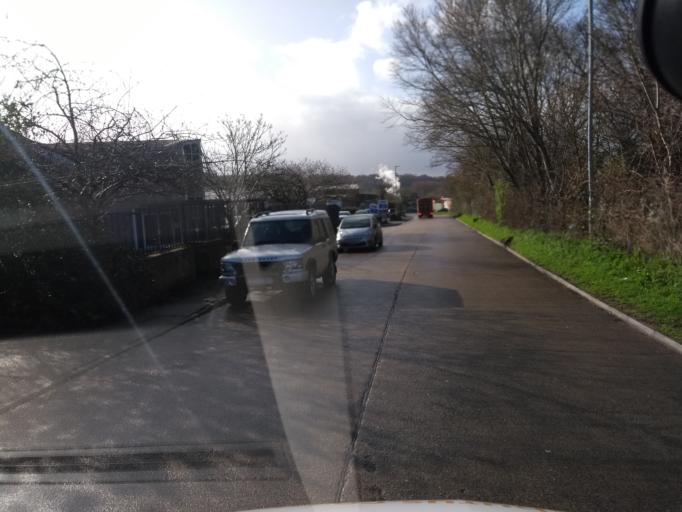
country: GB
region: England
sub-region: Somerset
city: Yeovil
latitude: 50.9510
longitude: -2.6066
